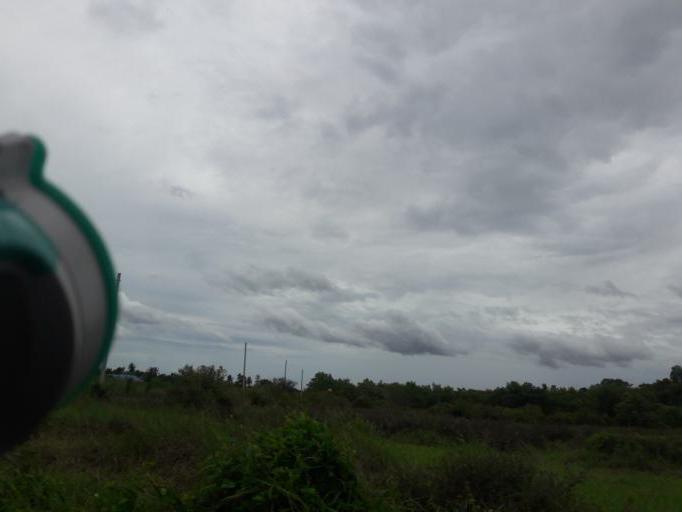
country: TH
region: Ratchaburi
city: Damnoen Saduak
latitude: 13.5279
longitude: 99.9743
